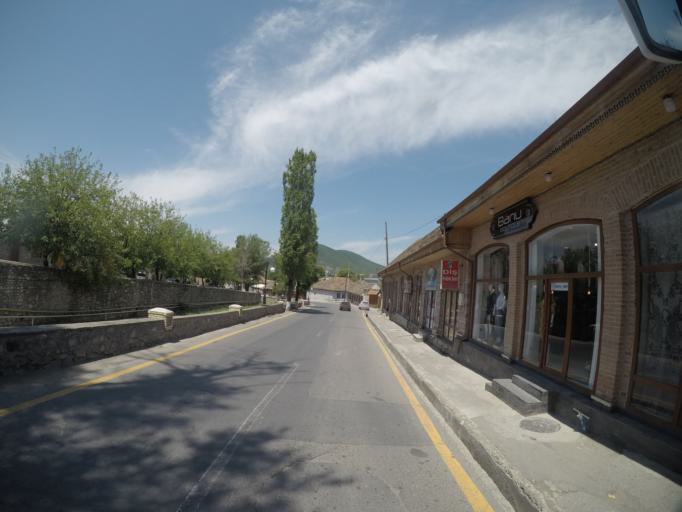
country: AZ
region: Shaki City
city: Sheki
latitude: 41.2008
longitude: 47.1853
